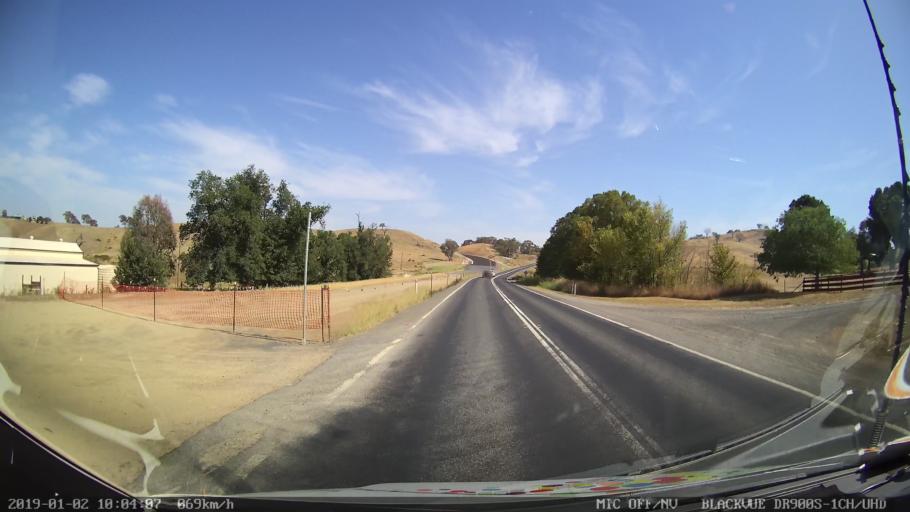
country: AU
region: New South Wales
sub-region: Gundagai
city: Gundagai
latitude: -35.1708
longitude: 148.1239
